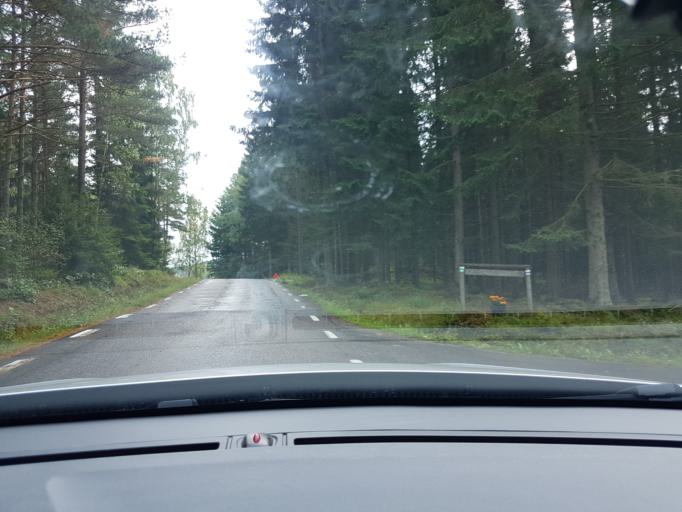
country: SE
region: Vaestra Goetaland
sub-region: Ale Kommun
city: Skepplanda
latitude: 57.8998
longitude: 12.1859
